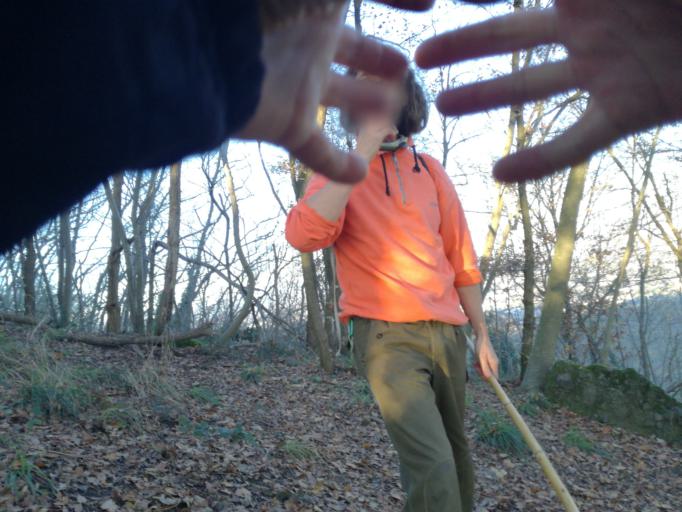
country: IT
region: Veneto
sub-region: Provincia di Padova
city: Battaglia Terme
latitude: 45.3086
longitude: 11.7768
